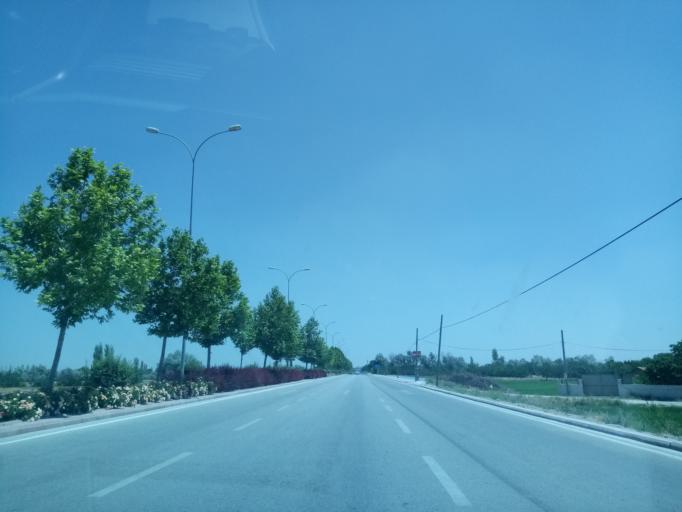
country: TR
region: Konya
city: Meram
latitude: 37.8165
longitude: 32.4505
